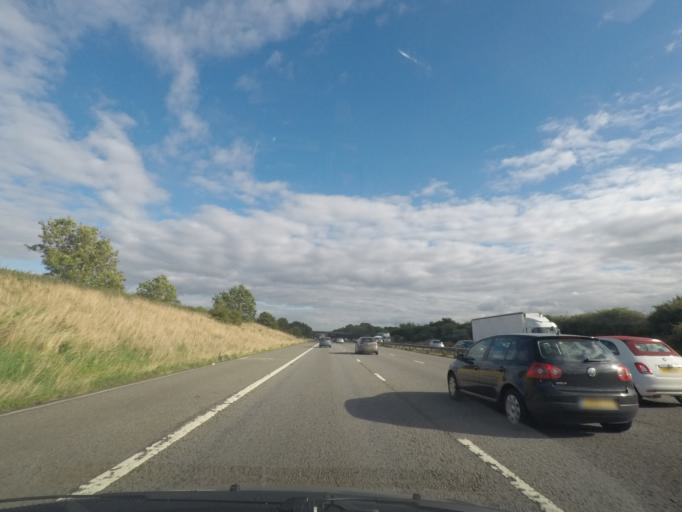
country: GB
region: England
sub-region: Leicestershire
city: Markfield
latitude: 52.6681
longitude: -1.2766
